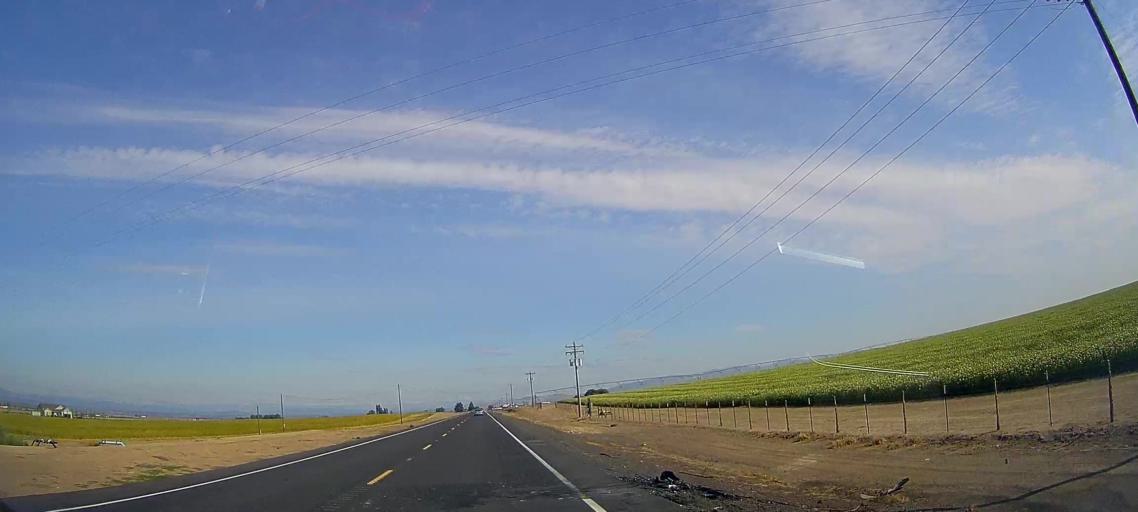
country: US
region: Oregon
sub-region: Jefferson County
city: Madras
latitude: 44.6828
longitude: -121.1490
